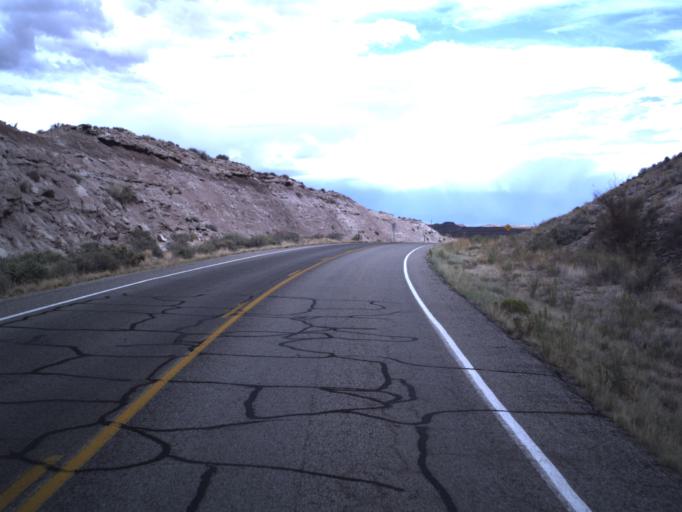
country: US
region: Utah
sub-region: San Juan County
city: Blanding
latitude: 37.2745
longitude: -109.3497
